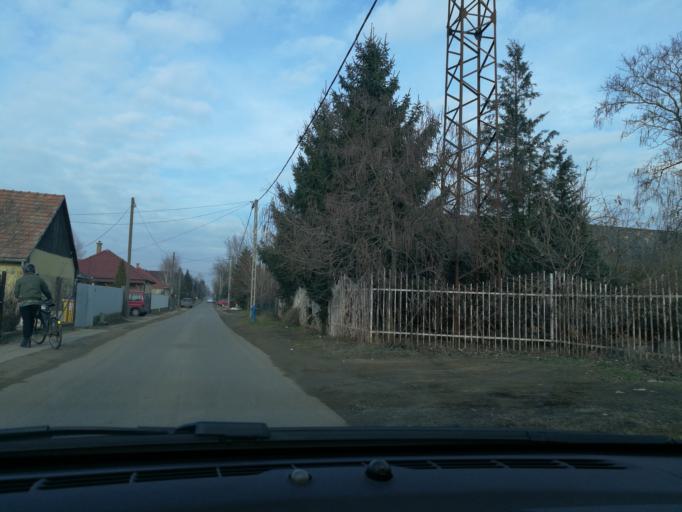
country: HU
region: Szabolcs-Szatmar-Bereg
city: Nyiregyhaza
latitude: 47.9341
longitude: 21.7371
